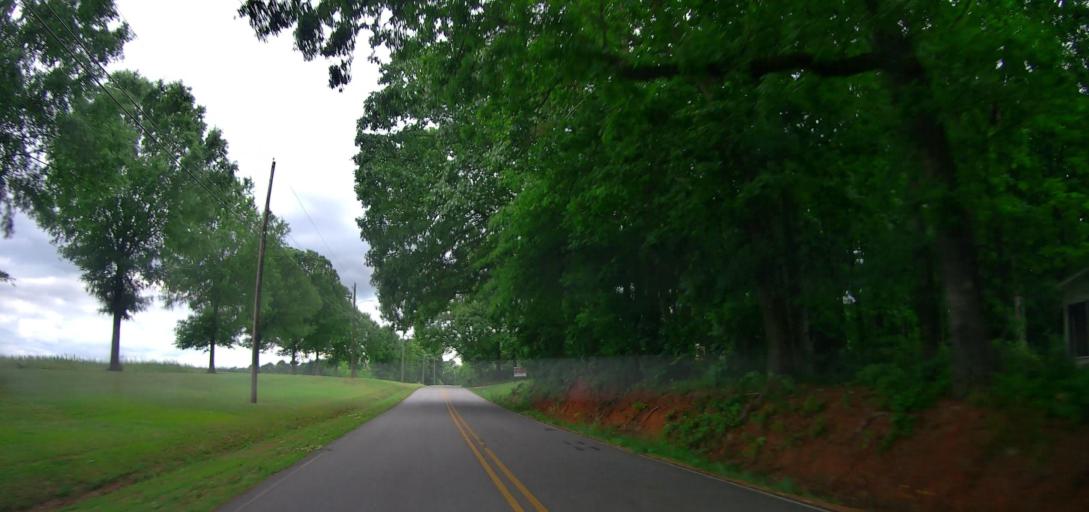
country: US
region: Georgia
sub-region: Walton County
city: Monroe
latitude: 33.8016
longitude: -83.6952
